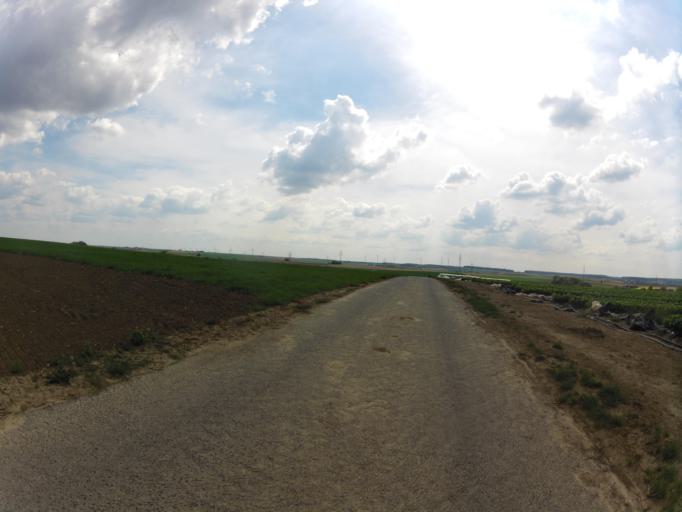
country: DE
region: Bavaria
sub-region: Regierungsbezirk Unterfranken
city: Sulzdorf
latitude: 49.6288
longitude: 9.9078
